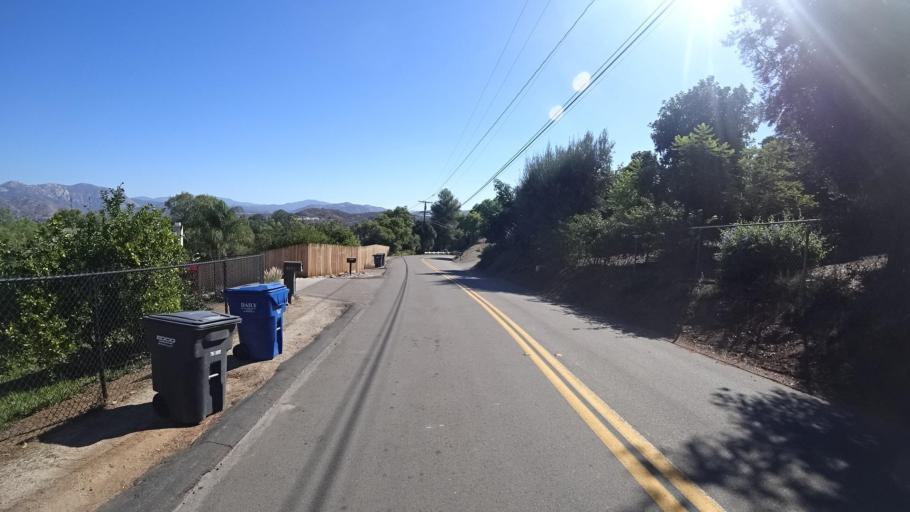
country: US
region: California
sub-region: San Diego County
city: Winter Gardens
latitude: 32.8393
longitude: -116.9417
